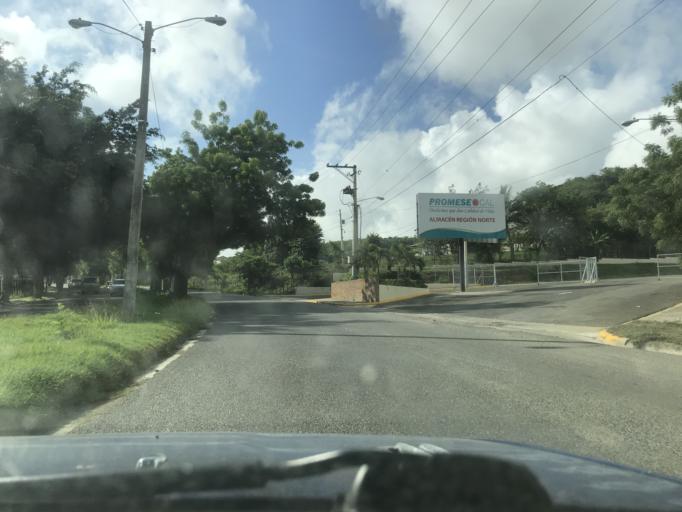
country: DO
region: Santiago
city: Santiago de los Caballeros
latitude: 19.4140
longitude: -70.7289
